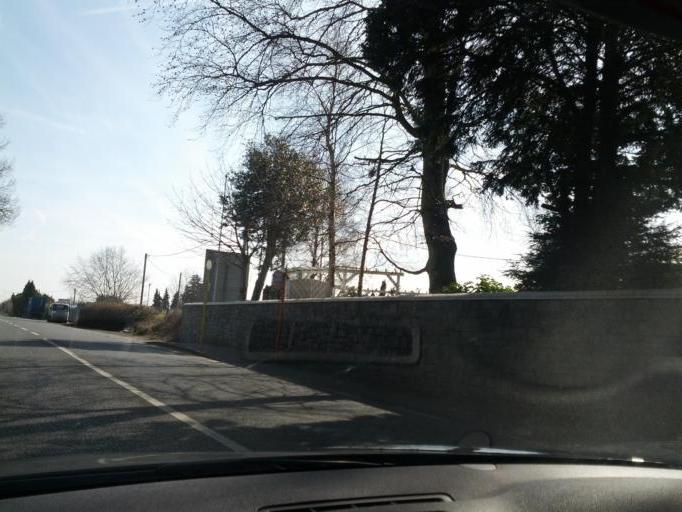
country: IE
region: Leinster
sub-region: Kildare
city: Leixlip
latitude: 53.3607
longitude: -6.4790
